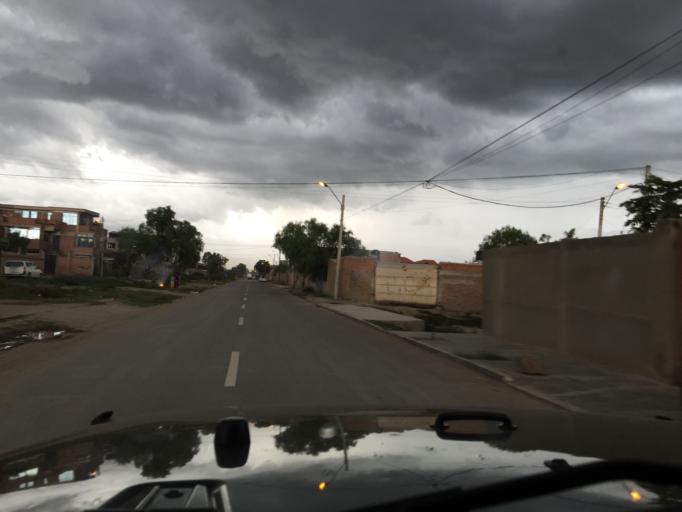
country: BO
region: Cochabamba
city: Cochabamba
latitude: -17.3998
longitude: -66.2103
